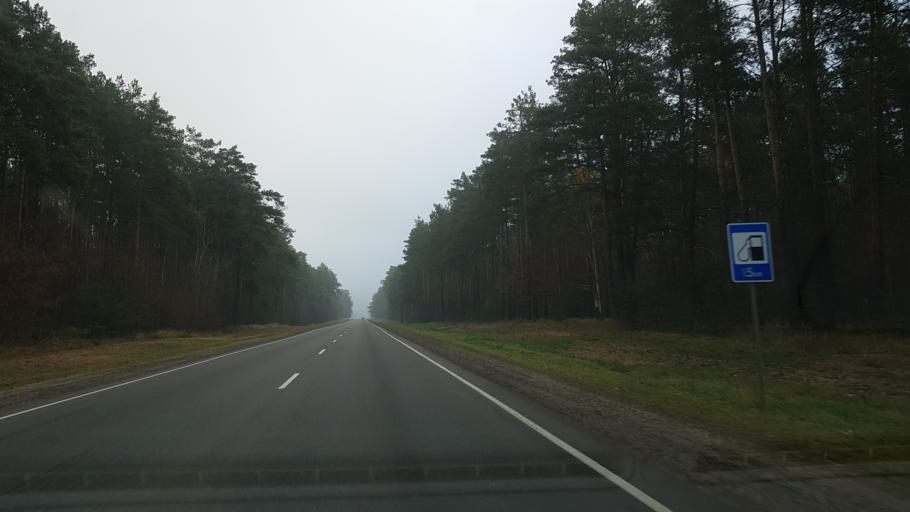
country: BY
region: Mogilev
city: Babruysk
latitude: 53.1627
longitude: 29.3255
